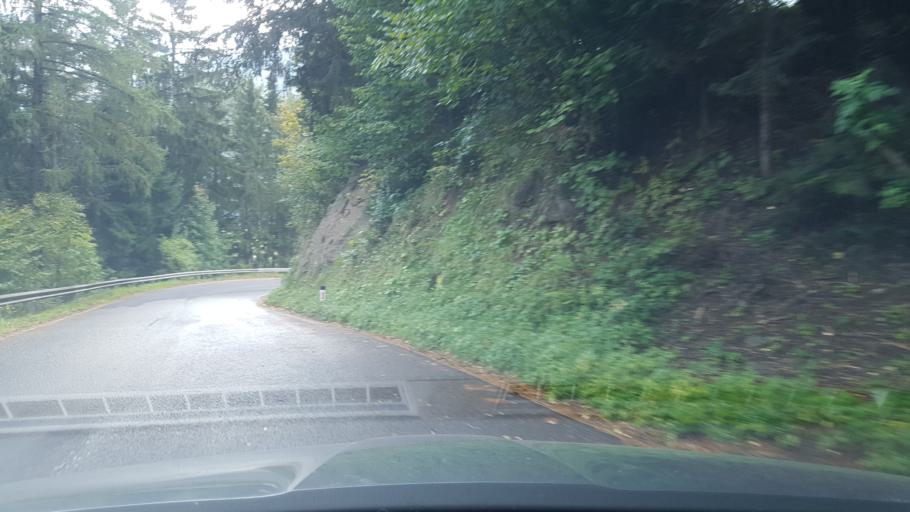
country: AT
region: Styria
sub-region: Politischer Bezirk Murau
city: Schoder
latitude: 47.1913
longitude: 14.1252
